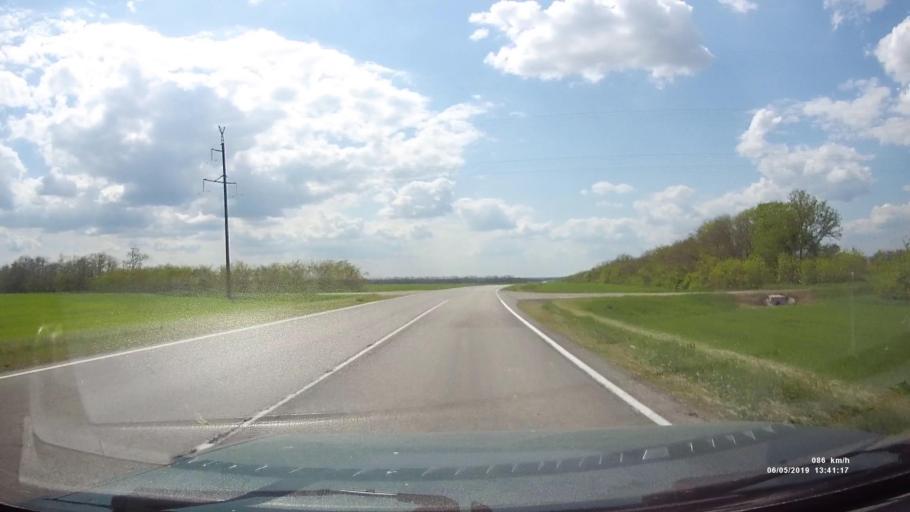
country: RU
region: Rostov
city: Ust'-Donetskiy
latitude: 47.6630
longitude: 40.6795
